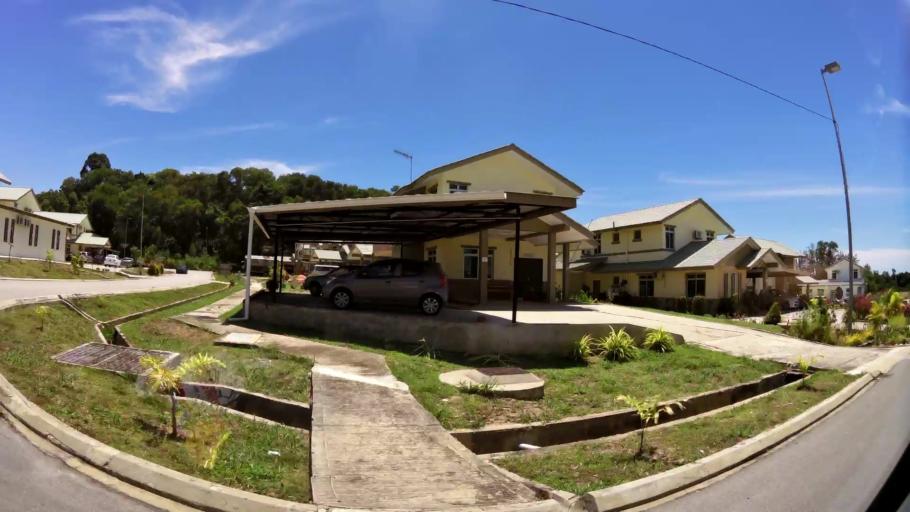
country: BN
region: Brunei and Muara
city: Bandar Seri Begawan
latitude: 5.0316
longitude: 115.0301
